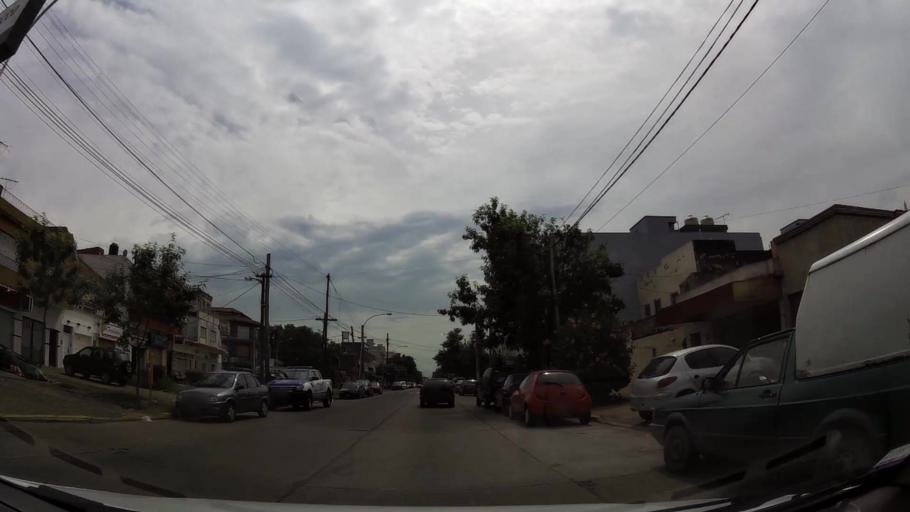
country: AR
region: Buenos Aires F.D.
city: Villa Lugano
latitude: -34.6951
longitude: -58.5036
